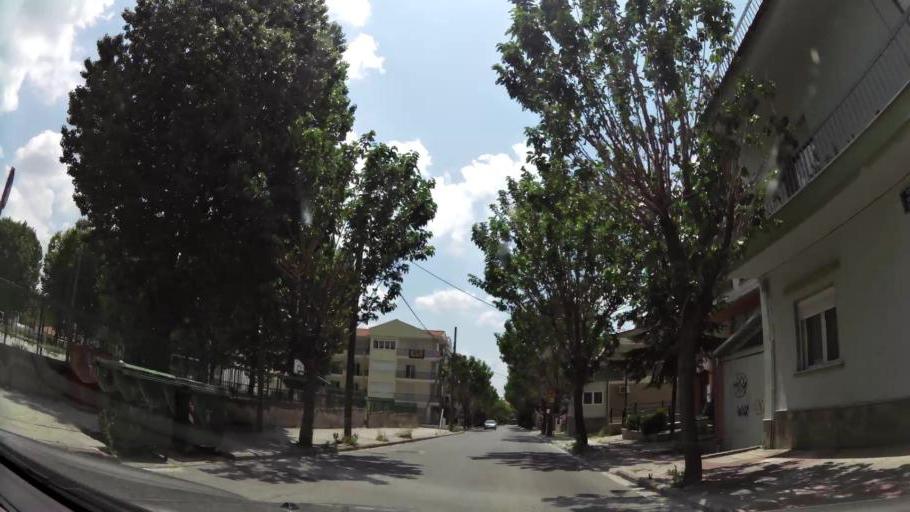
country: GR
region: West Macedonia
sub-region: Nomos Kozanis
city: Kozani
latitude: 40.2958
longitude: 21.7980
